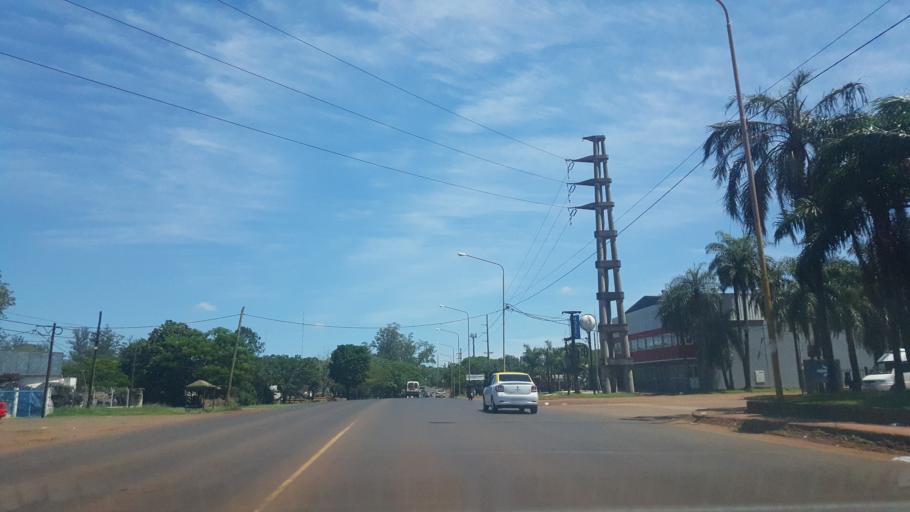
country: AR
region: Misiones
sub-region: Departamento de Capital
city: Posadas
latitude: -27.4023
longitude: -55.9218
